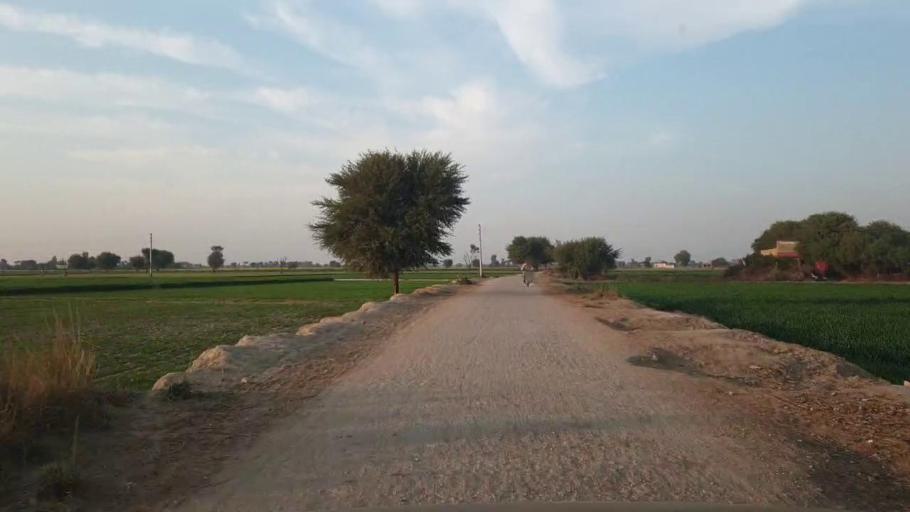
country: PK
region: Sindh
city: Shahpur Chakar
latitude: 26.1853
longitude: 68.6171
